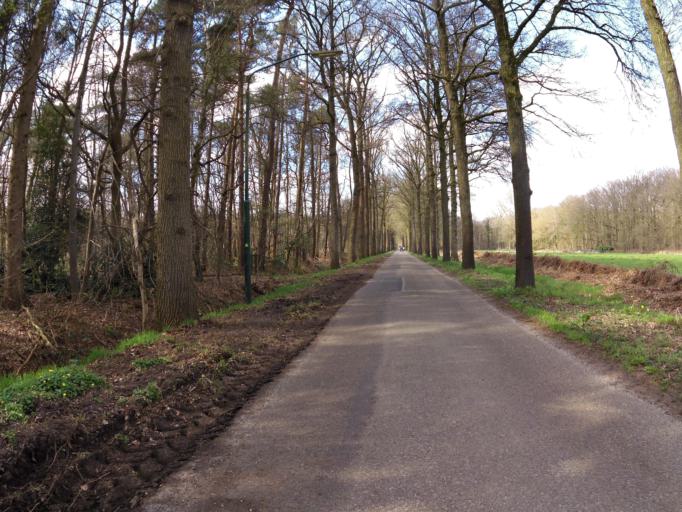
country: NL
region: North Brabant
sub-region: Gemeente Oisterwijk
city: Oisterwijk
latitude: 51.6305
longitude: 5.1758
